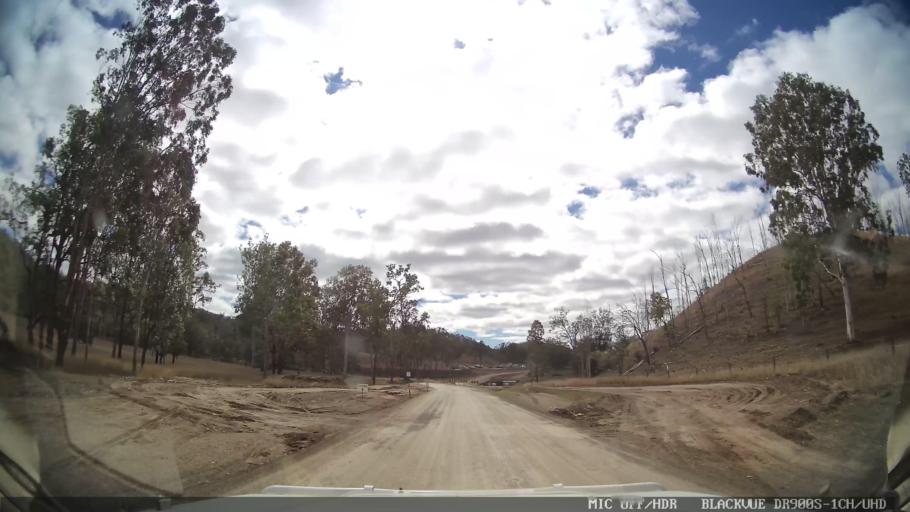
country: AU
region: Queensland
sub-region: Gladstone
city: Toolooa
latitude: -24.6161
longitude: 151.2988
